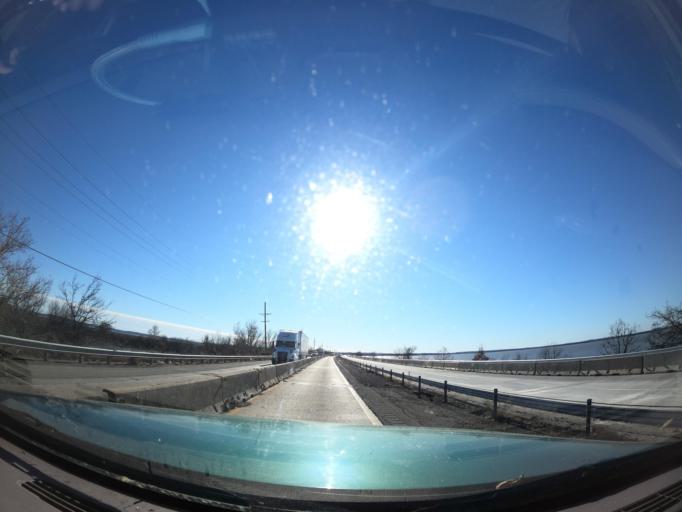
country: US
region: Oklahoma
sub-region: McIntosh County
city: Eufaula
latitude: 35.3494
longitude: -95.5788
